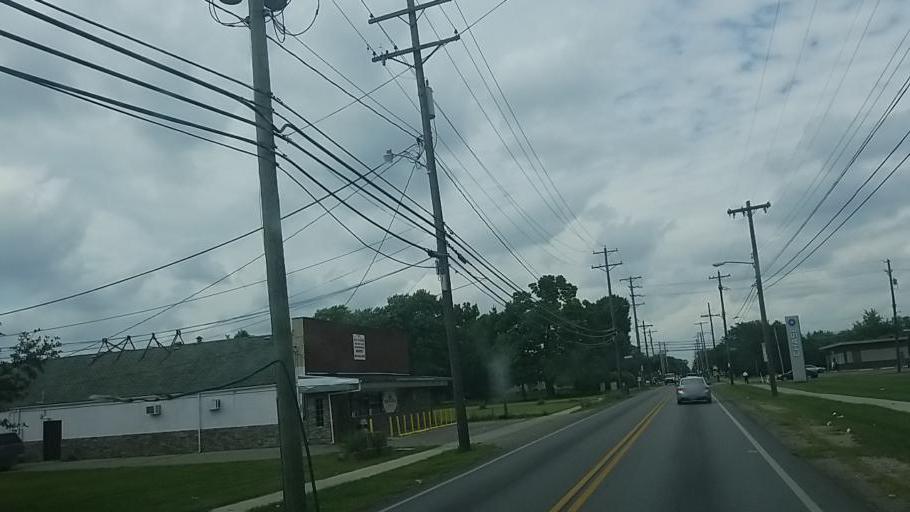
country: US
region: Ohio
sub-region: Franklin County
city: Columbus
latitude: 39.9314
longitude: -82.9646
